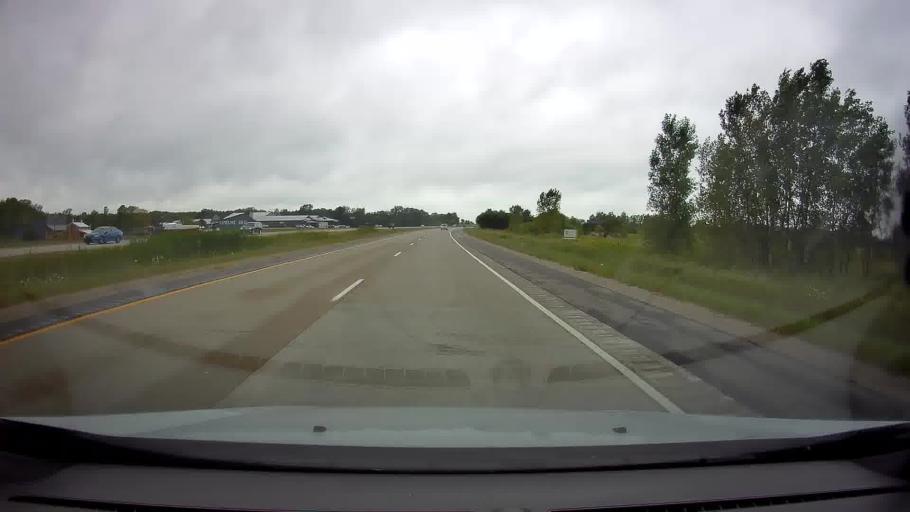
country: US
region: Wisconsin
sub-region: Shawano County
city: Bonduel
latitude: 44.7038
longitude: -88.3702
